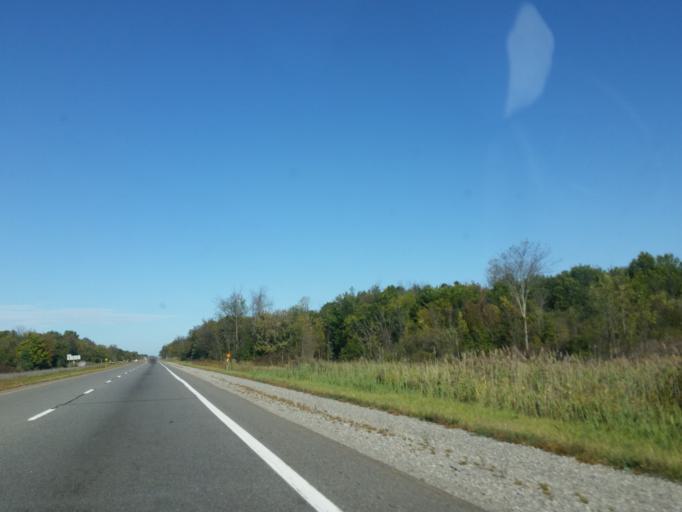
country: US
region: New York
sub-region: Niagara County
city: Niagara Falls
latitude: 43.0048
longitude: -79.0754
